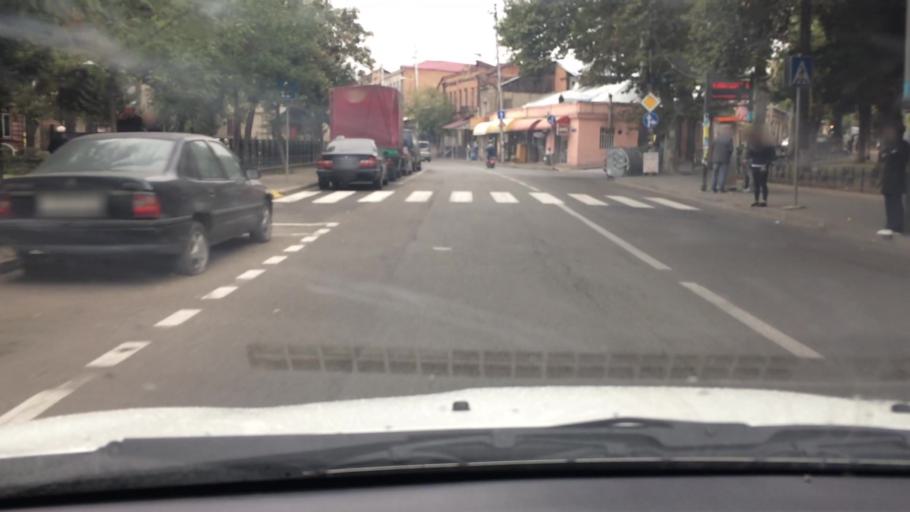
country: GE
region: T'bilisi
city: Tbilisi
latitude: 41.7057
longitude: 44.8056
